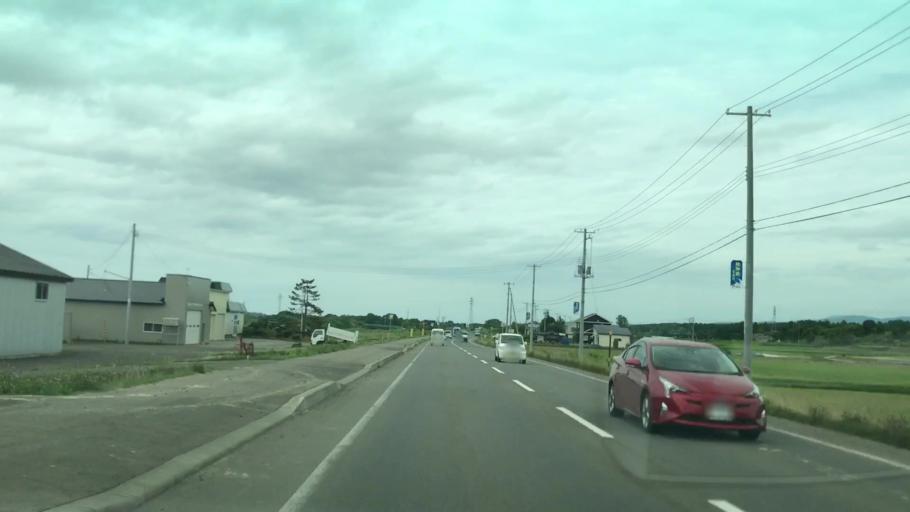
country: JP
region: Hokkaido
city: Iwanai
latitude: 42.9813
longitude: 140.6209
